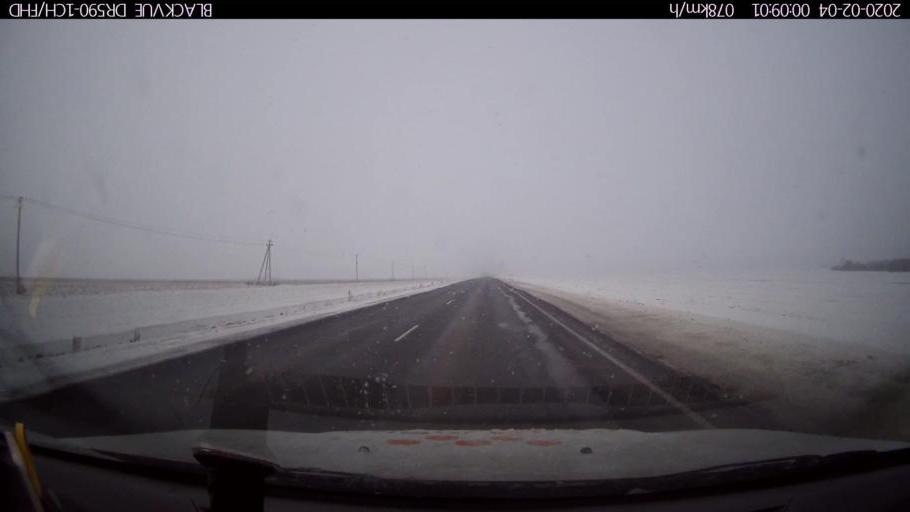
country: RU
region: Nizjnij Novgorod
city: Dal'neye Konstantinovo
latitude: 55.8770
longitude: 44.1362
